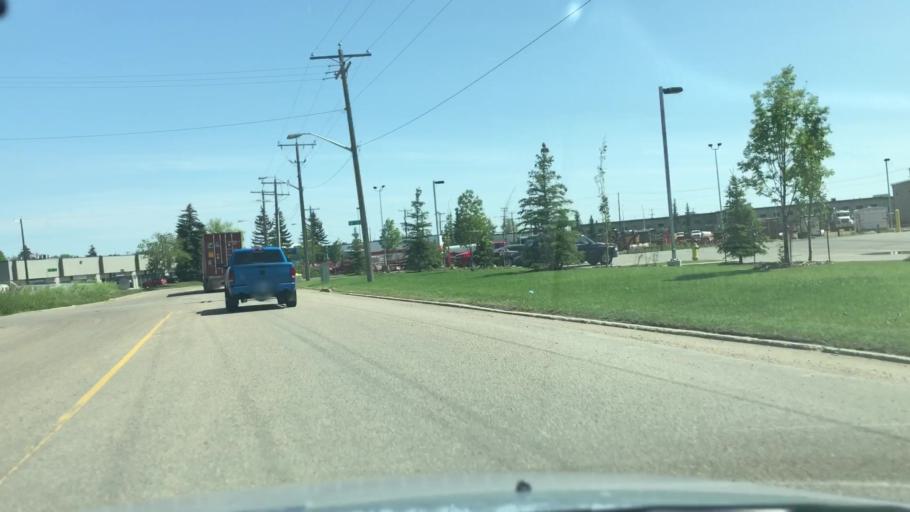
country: CA
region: Alberta
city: St. Albert
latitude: 53.5850
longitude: -113.5813
